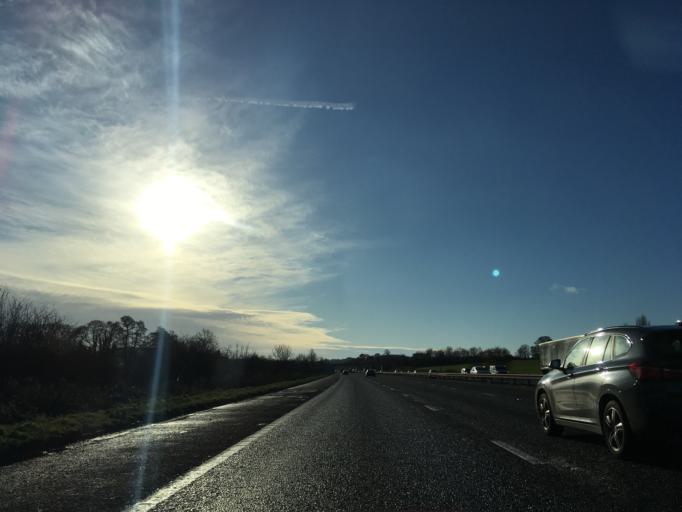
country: GB
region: England
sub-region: South Gloucestershire
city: Falfield
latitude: 51.6321
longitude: -2.4567
